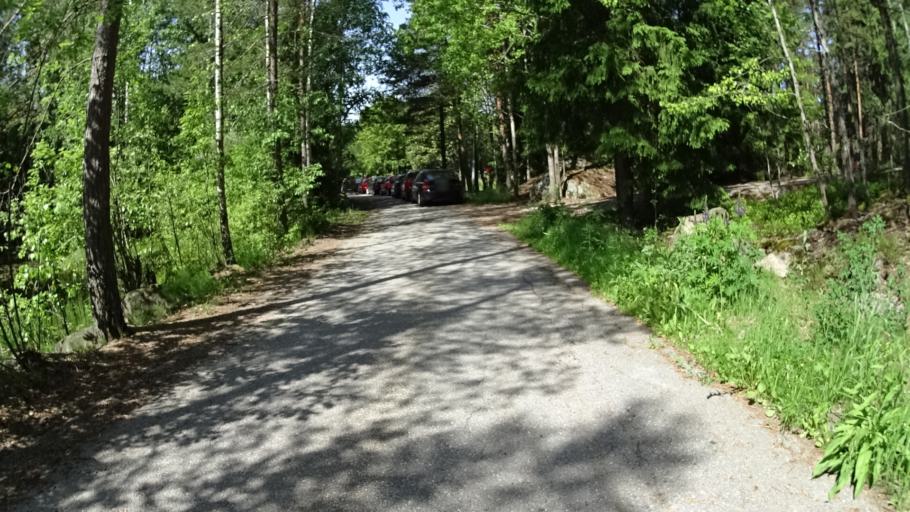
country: FI
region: Uusimaa
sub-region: Helsinki
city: Kauniainen
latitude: 60.3245
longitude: 24.7321
